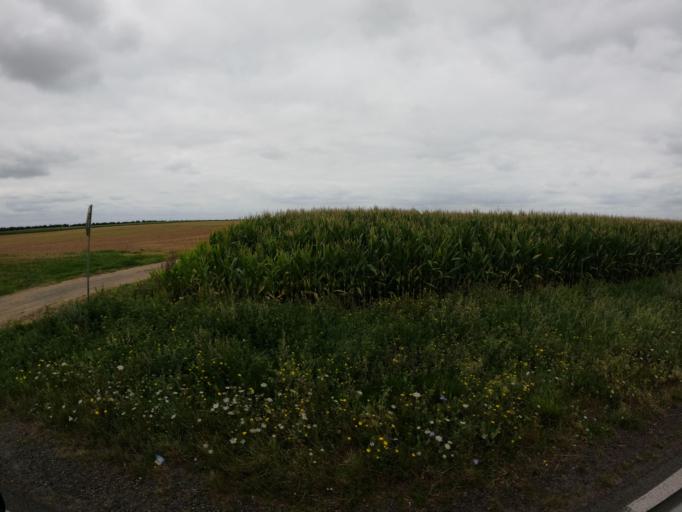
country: FR
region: Pays de la Loire
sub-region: Departement de la Vendee
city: Serigne
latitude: 46.4848
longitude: -0.8913
